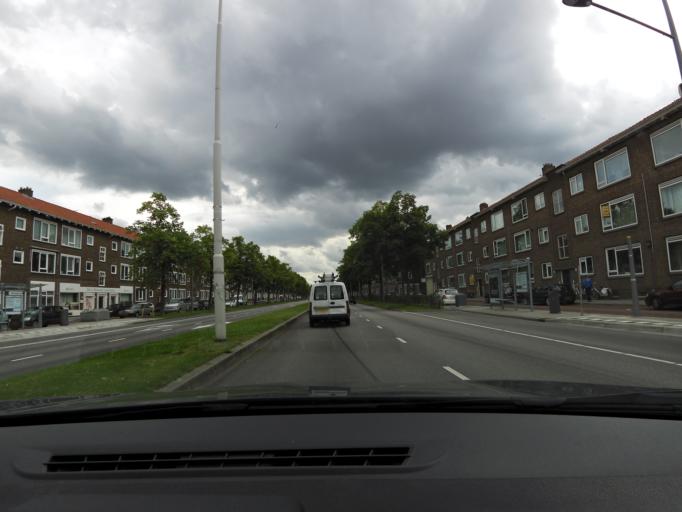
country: NL
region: South Holland
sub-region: Gemeente Rotterdam
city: Delfshaven
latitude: 51.8883
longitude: 4.4720
